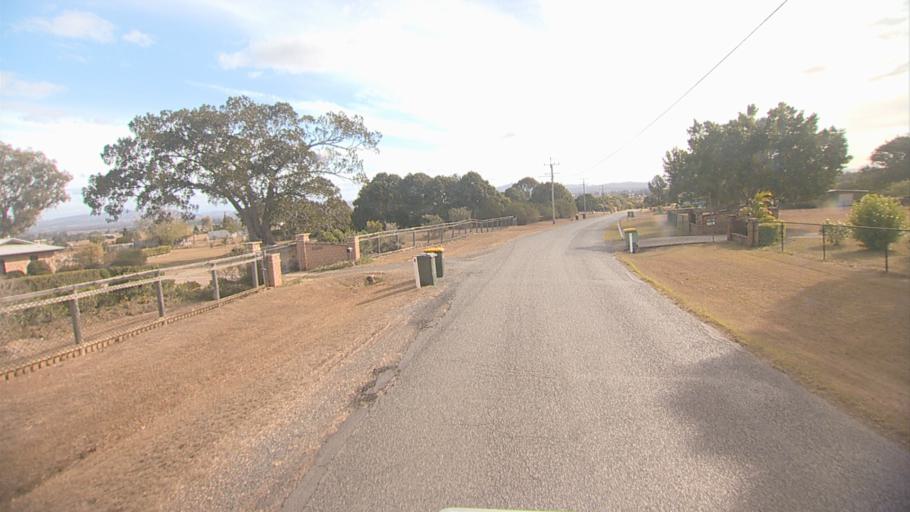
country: AU
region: Queensland
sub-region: Logan
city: Cedar Vale
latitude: -27.9153
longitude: 152.9914
